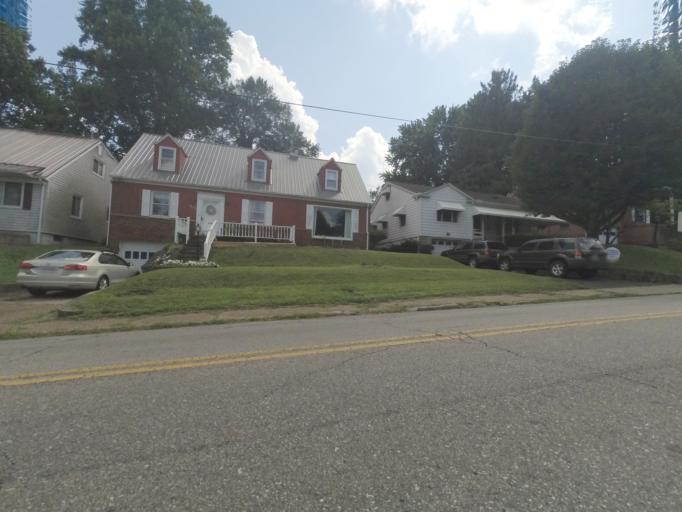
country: US
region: West Virginia
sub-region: Cabell County
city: Huntington
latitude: 38.4063
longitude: -82.4019
